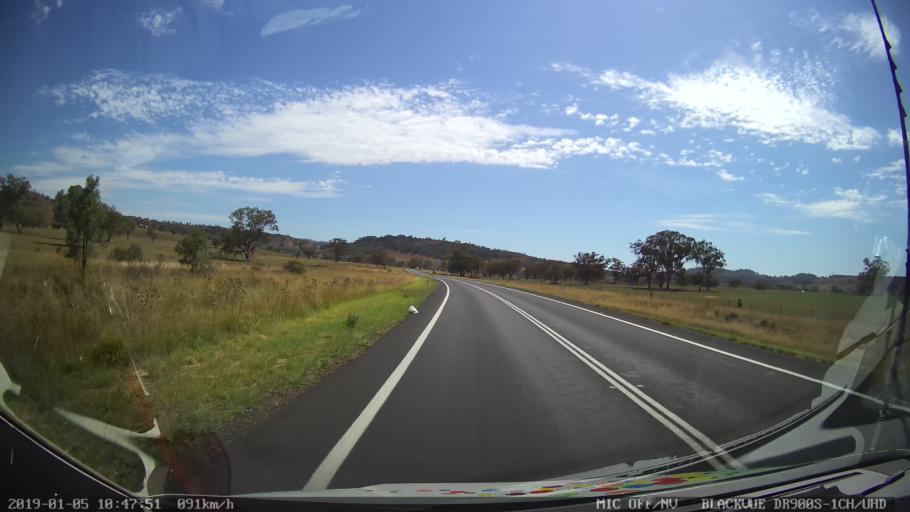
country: AU
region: New South Wales
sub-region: Warrumbungle Shire
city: Coonabarabran
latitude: -31.4415
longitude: 149.0384
